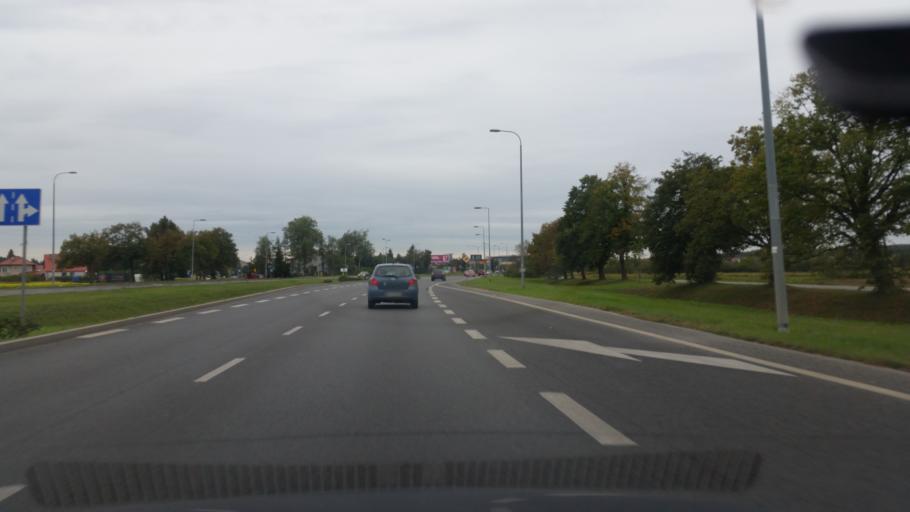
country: PL
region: Masovian Voivodeship
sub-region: Warszawa
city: Kabaty
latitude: 52.1358
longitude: 21.0998
